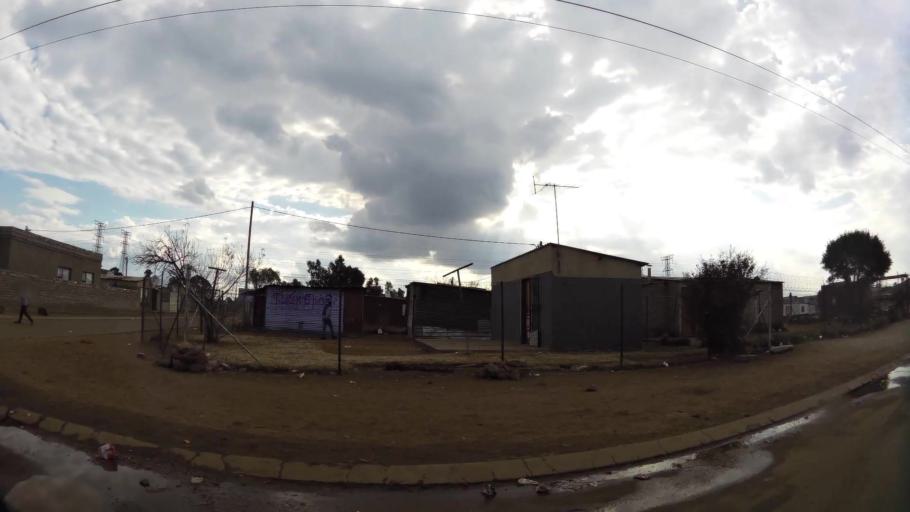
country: ZA
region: Gauteng
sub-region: Sedibeng District Municipality
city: Vanderbijlpark
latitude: -26.6742
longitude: 27.8561
